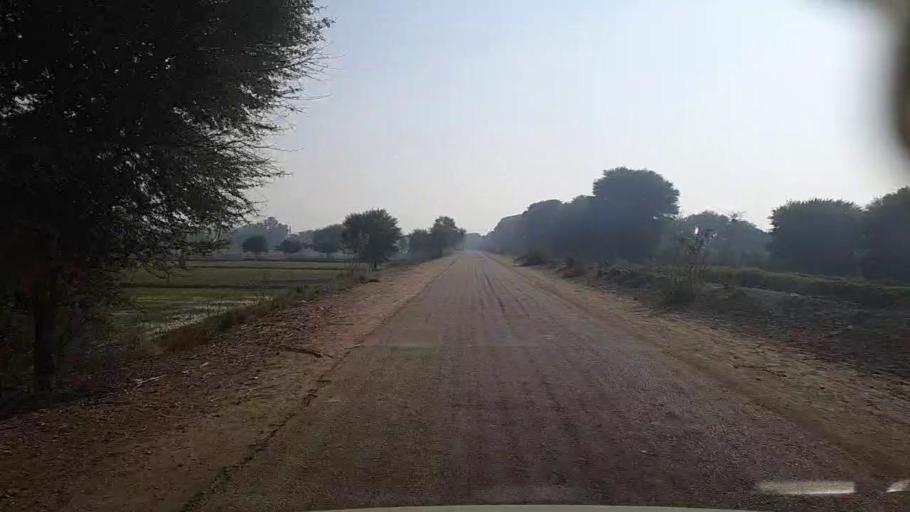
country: PK
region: Sindh
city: Kandiari
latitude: 26.8414
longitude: 68.4893
